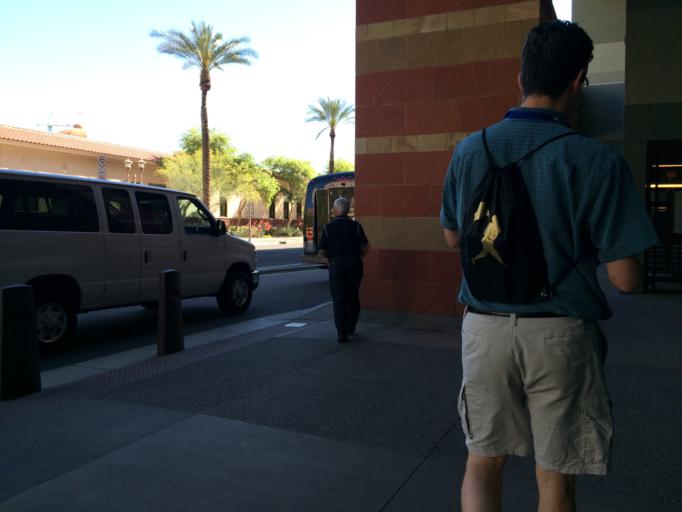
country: US
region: Arizona
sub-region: Maricopa County
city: Phoenix
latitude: 33.4506
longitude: -112.0691
